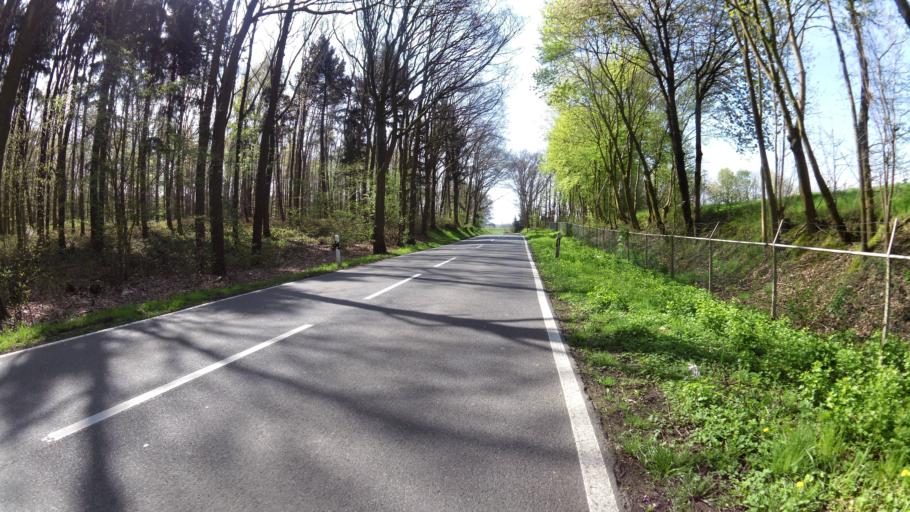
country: DE
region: North Rhine-Westphalia
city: Geilenkirchen
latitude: 50.9922
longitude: 6.0705
